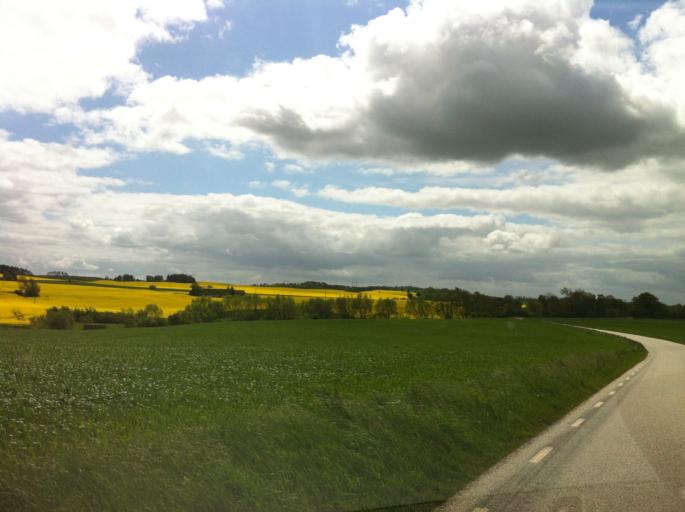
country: SE
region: Skane
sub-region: Svalovs Kommun
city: Teckomatorp
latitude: 55.8516
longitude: 13.0780
